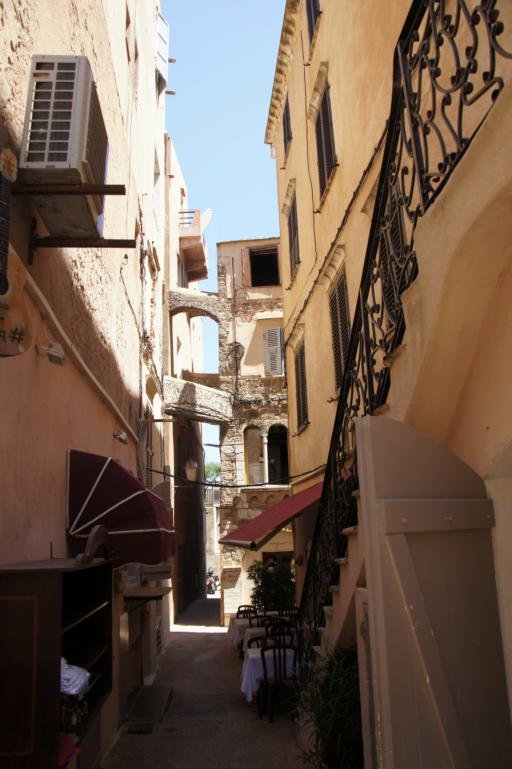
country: FR
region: Corsica
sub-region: Departement de la Corse-du-Sud
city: Bonifacio
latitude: 41.3869
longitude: 9.1586
